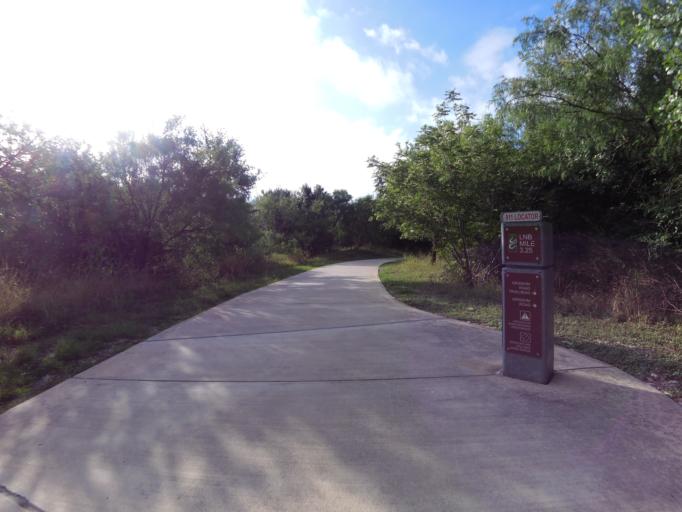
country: US
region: Texas
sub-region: Bexar County
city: Leon Valley
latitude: 29.4818
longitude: -98.6318
